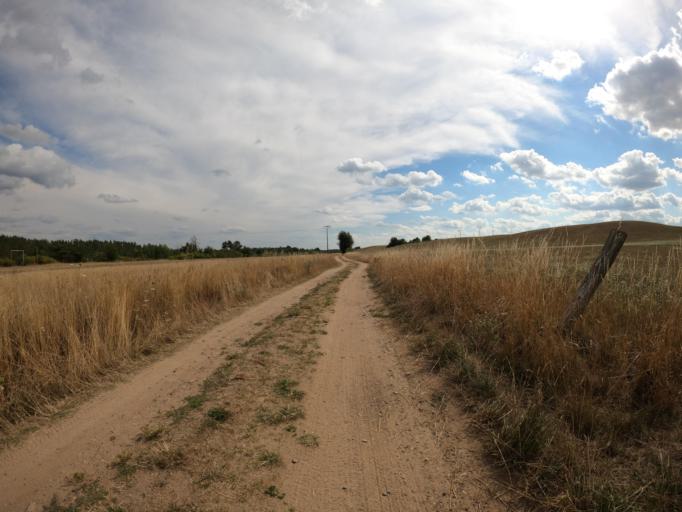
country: DE
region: Mecklenburg-Vorpommern
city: Loitz
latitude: 53.3242
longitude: 13.4287
